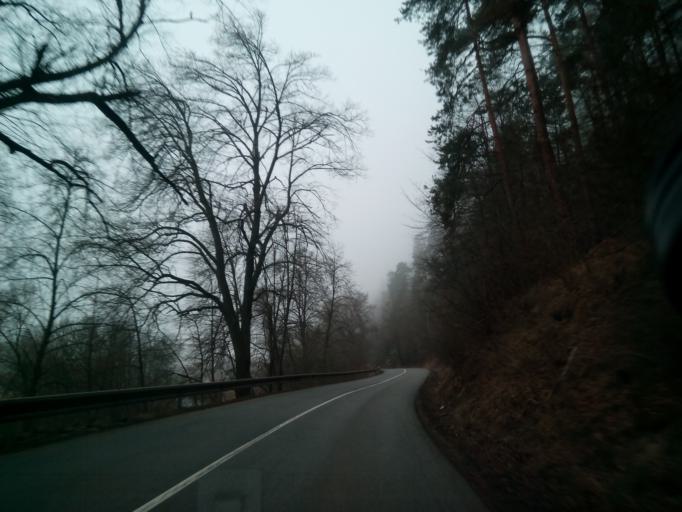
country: SK
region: Kosicky
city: Krompachy
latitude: 48.9370
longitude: 20.8314
